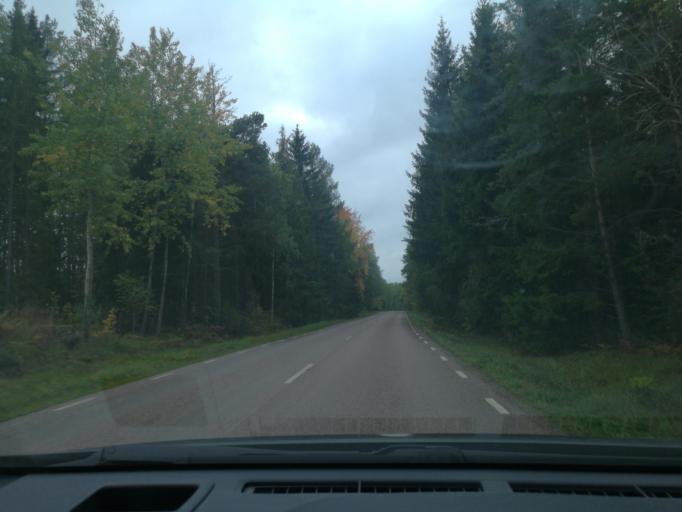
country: SE
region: Vaestmanland
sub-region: Vasteras
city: Tillberga
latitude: 59.7196
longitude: 16.6645
